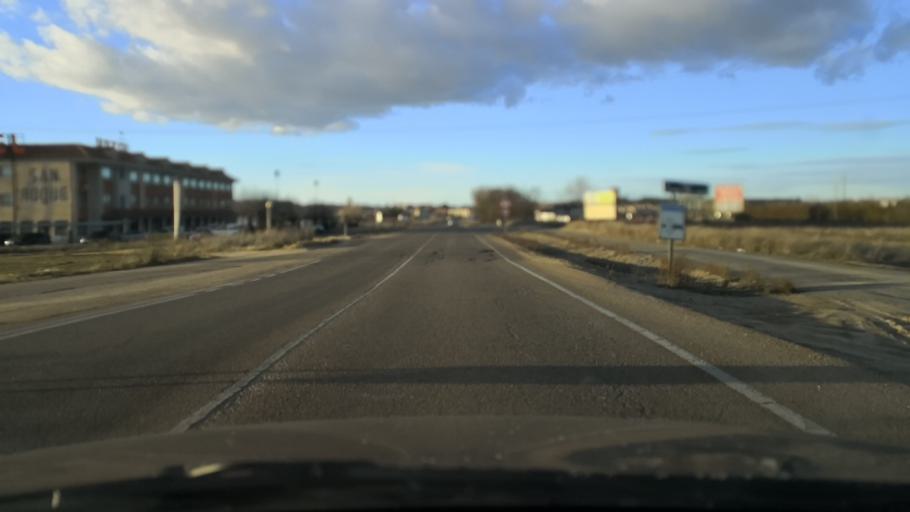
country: ES
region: Castille and Leon
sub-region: Provincia de Valladolid
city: Medina del Campo
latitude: 41.2953
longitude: -4.9033
